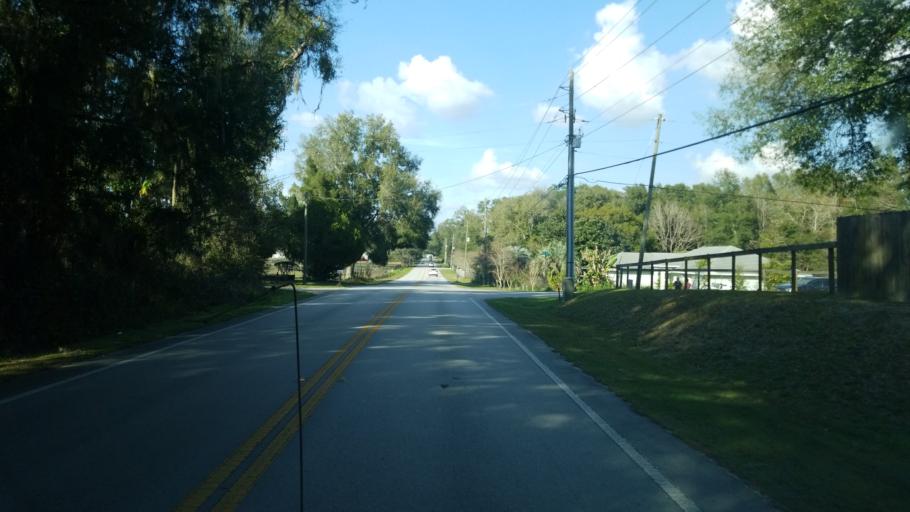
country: US
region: Florida
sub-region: Marion County
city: Ocala
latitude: 29.1716
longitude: -82.2518
